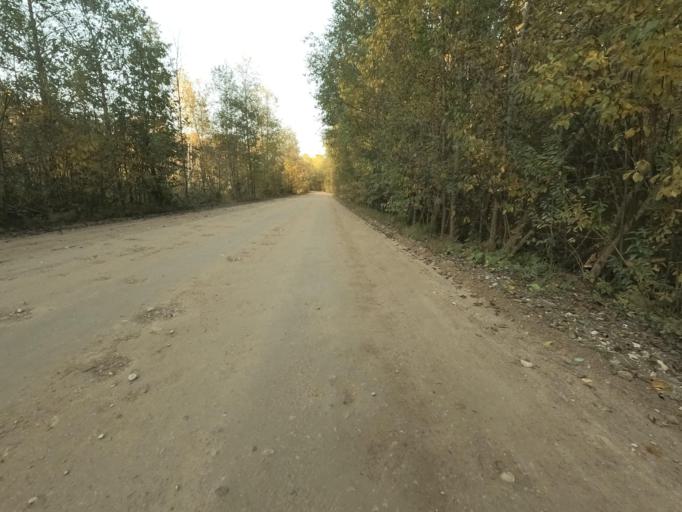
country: RU
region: Leningrad
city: Lyuban'
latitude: 58.9905
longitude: 31.1037
